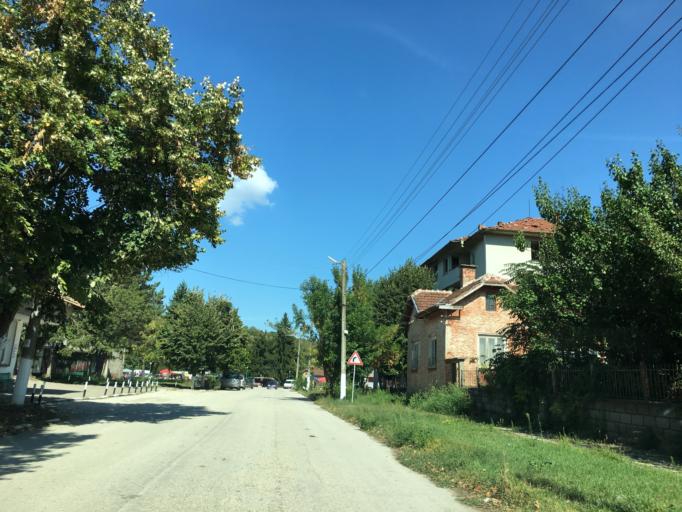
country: RO
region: Olt
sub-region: Comuna Orlea
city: Orlea
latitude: 43.6468
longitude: 24.4005
